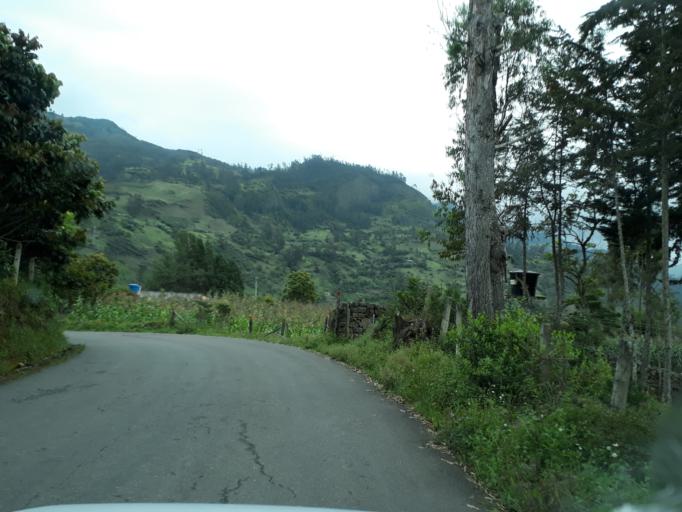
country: CO
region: Cundinamarca
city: Junin
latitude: 4.8172
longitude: -73.6767
